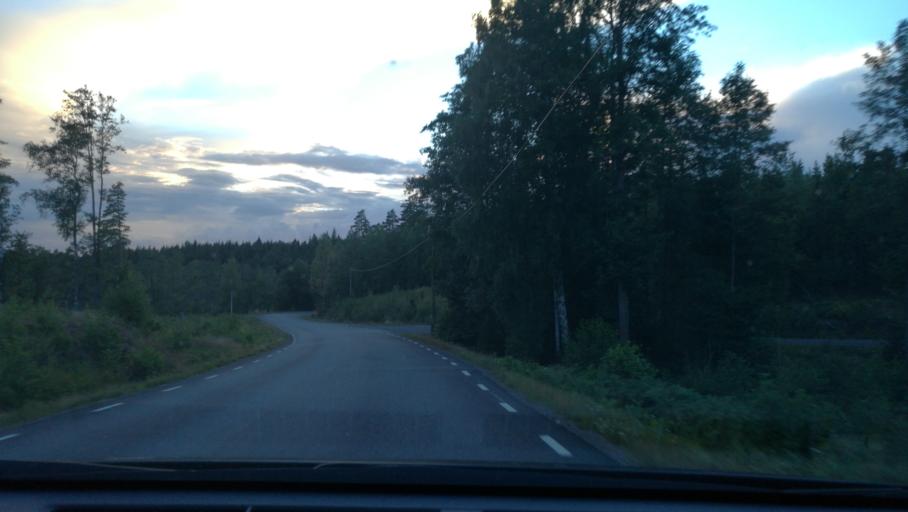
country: SE
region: OEstergoetland
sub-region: Norrkopings Kommun
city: Jursla
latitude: 58.8051
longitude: 16.1258
